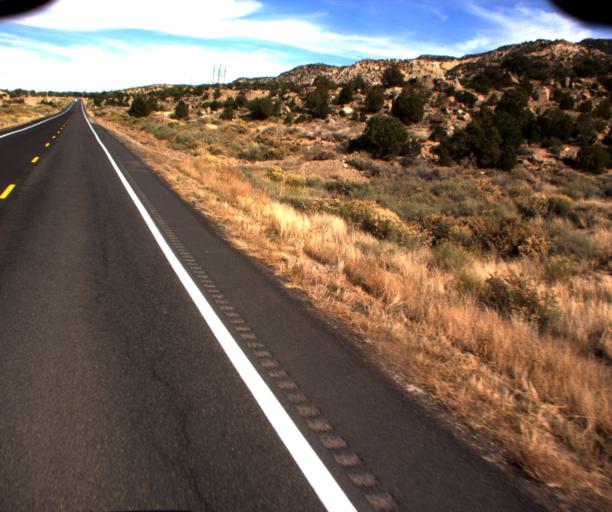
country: US
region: Arizona
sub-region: Navajo County
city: Kayenta
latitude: 36.6347
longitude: -110.4463
